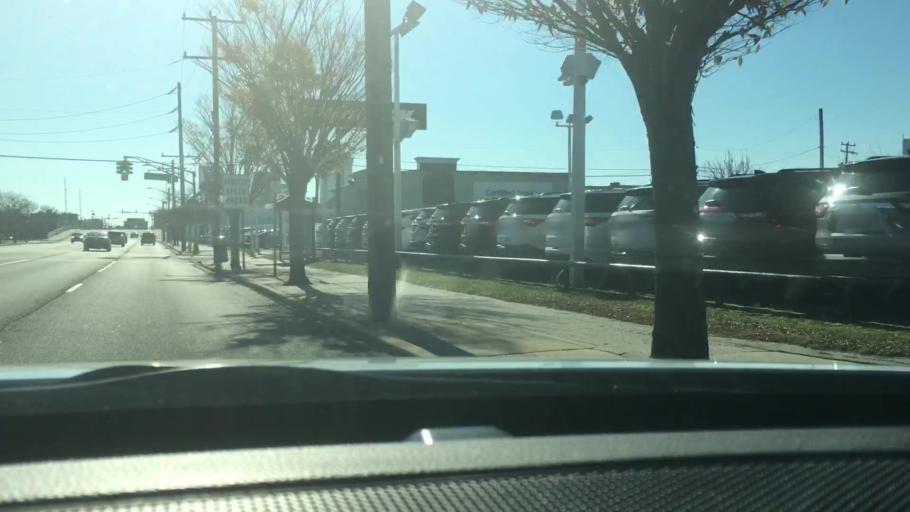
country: US
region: New Jersey
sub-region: Atlantic County
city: Ventnor City
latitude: 39.3561
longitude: -74.4589
